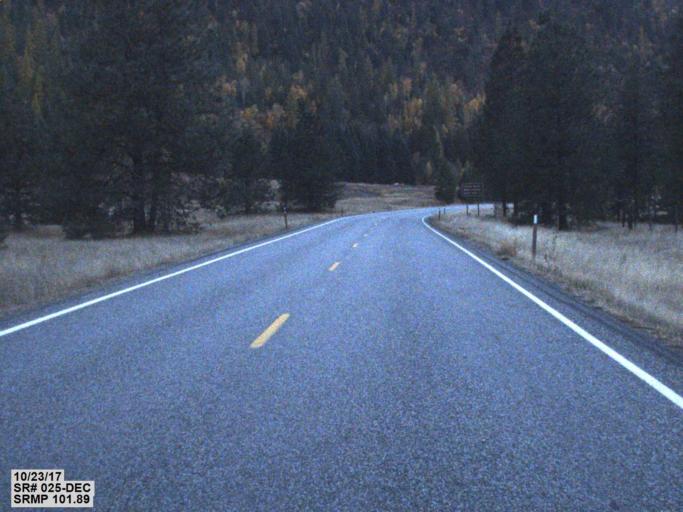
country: US
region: Washington
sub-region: Stevens County
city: Kettle Falls
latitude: 48.8098
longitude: -117.9461
